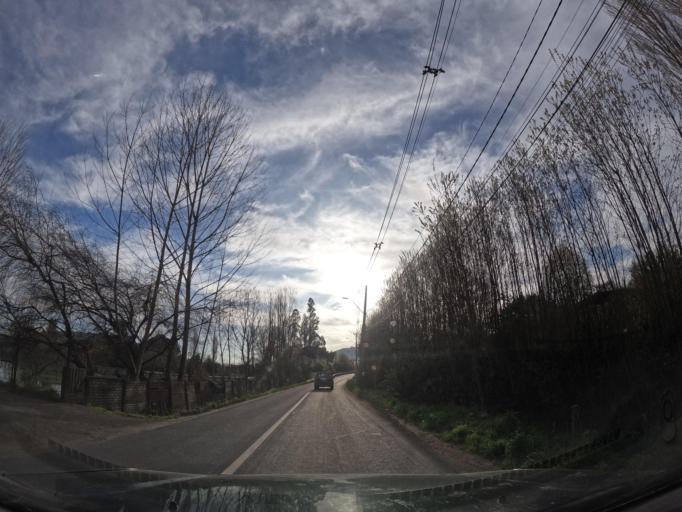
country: CL
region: Biobio
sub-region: Provincia de Concepcion
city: Chiguayante
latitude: -36.9811
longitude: -72.9366
